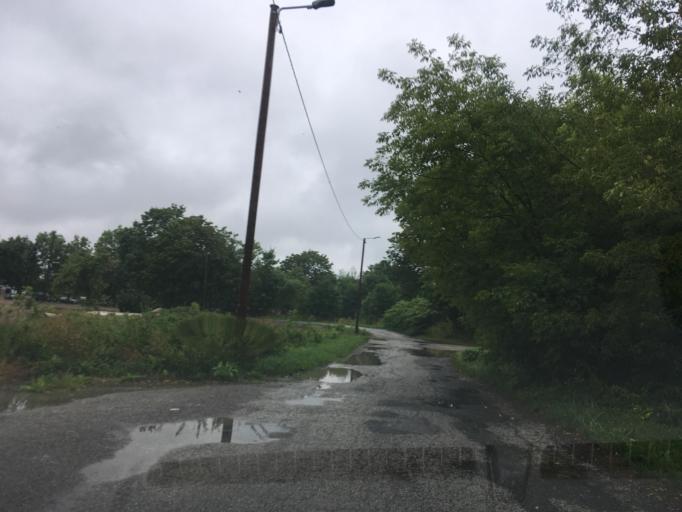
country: EE
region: Ida-Virumaa
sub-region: Kivioli linn
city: Kivioli
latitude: 59.3579
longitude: 26.9623
